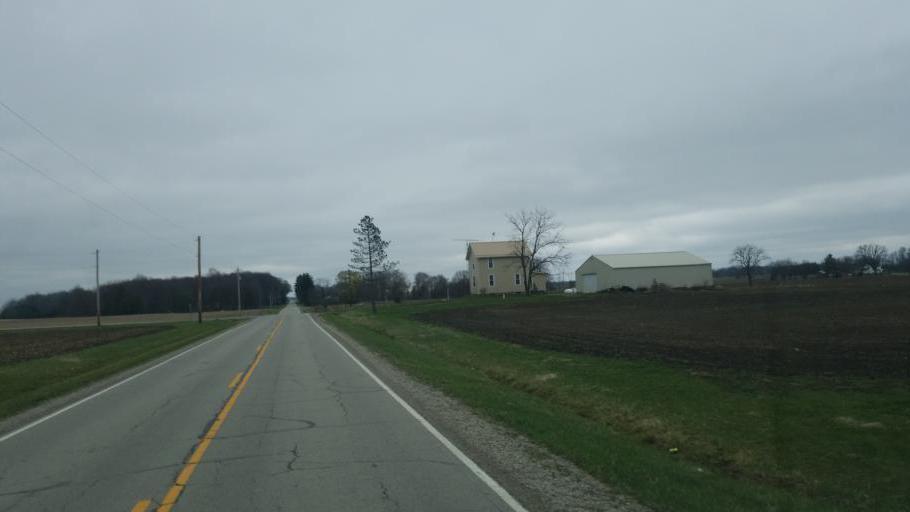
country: US
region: Ohio
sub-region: Crawford County
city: Bucyrus
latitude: 40.8193
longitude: -83.0557
